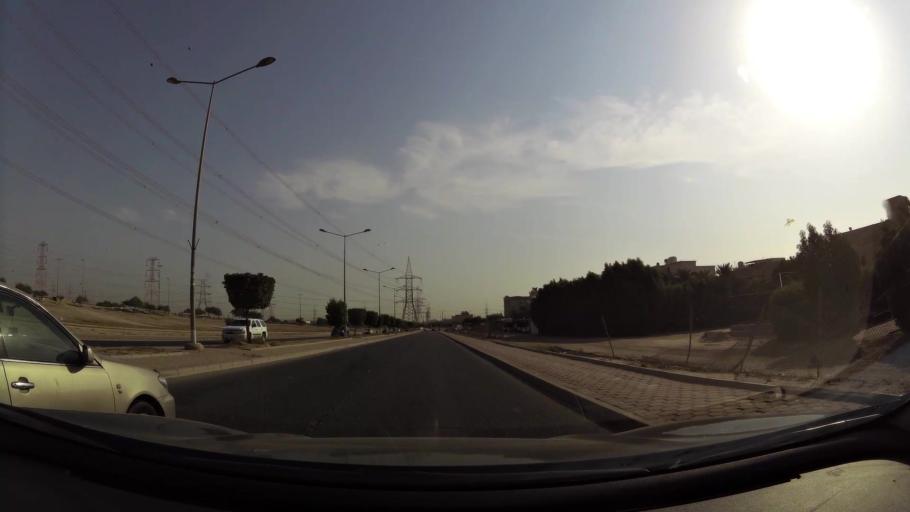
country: KW
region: Mubarak al Kabir
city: Mubarak al Kabir
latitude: 29.1718
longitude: 48.0576
